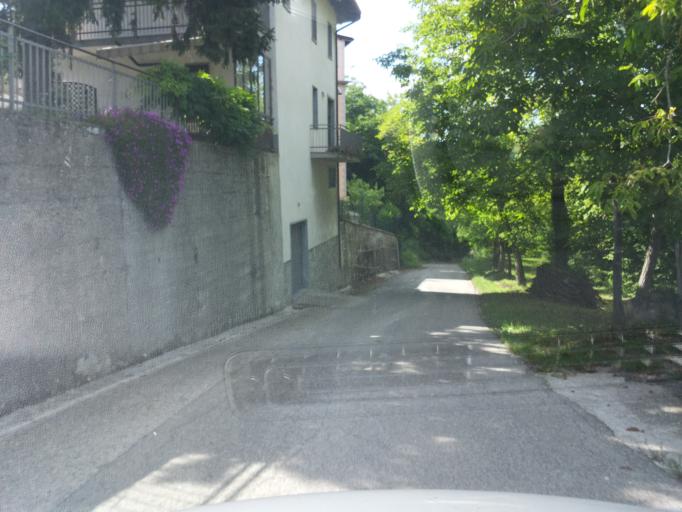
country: IT
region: Piedmont
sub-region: Provincia di Alessandria
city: Serralunga di Crea
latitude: 45.1025
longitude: 8.2755
